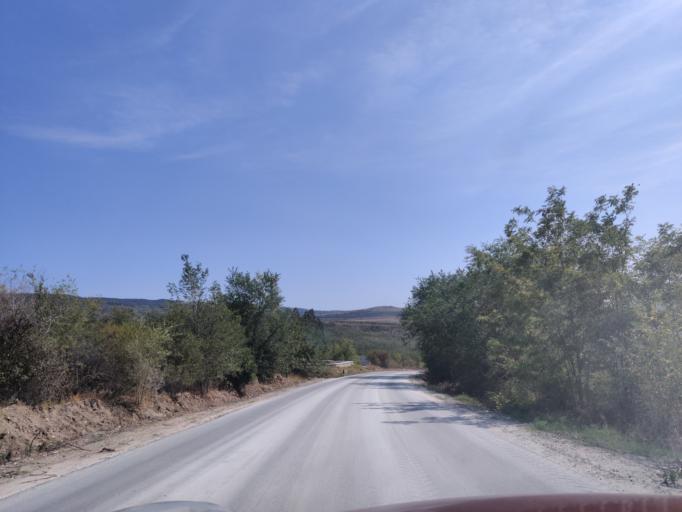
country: MD
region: Ungheni
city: Ungheni
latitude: 47.2566
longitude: 27.9949
